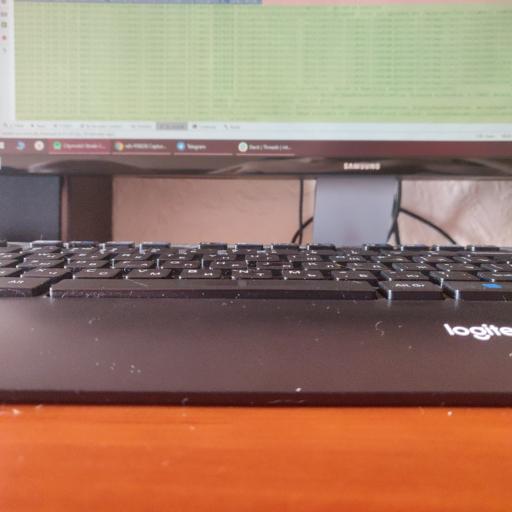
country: AX
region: Alands skaergard
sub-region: Vardoe
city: Vardoe
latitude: 60.8030
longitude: 20.4451
